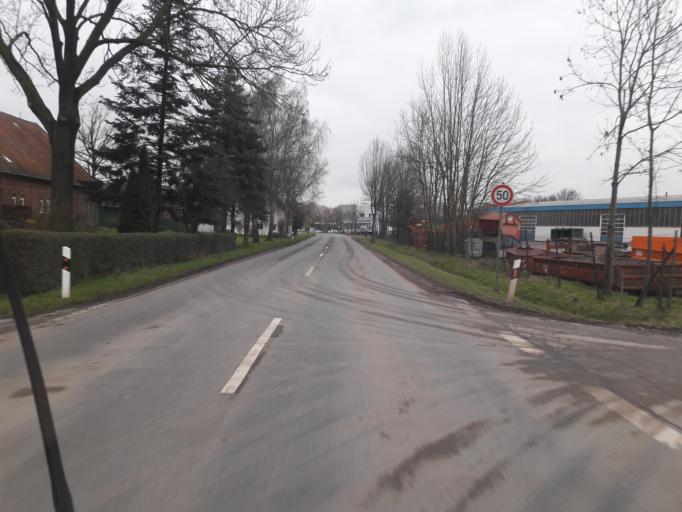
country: DE
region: North Rhine-Westphalia
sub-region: Regierungsbezirk Detmold
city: Minden
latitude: 52.3595
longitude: 8.8515
